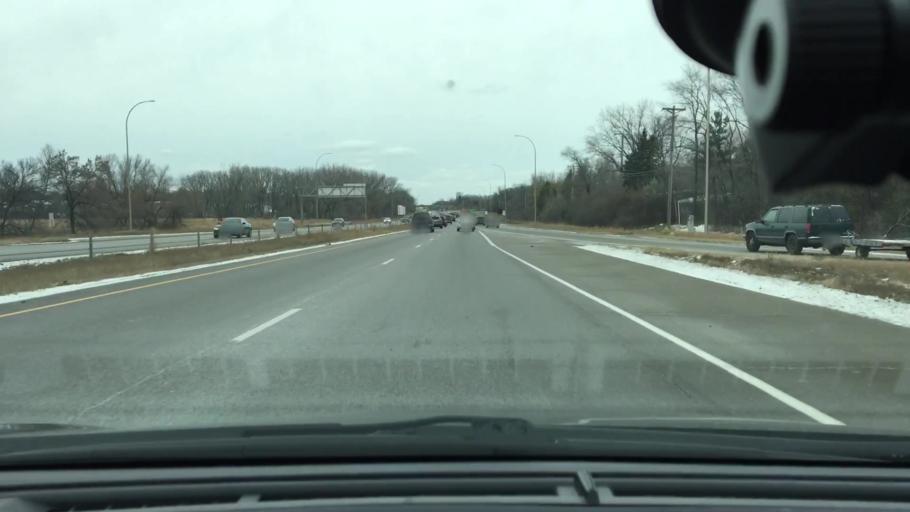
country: US
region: Minnesota
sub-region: Hennepin County
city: New Hope
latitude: 45.0604
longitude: -93.4007
